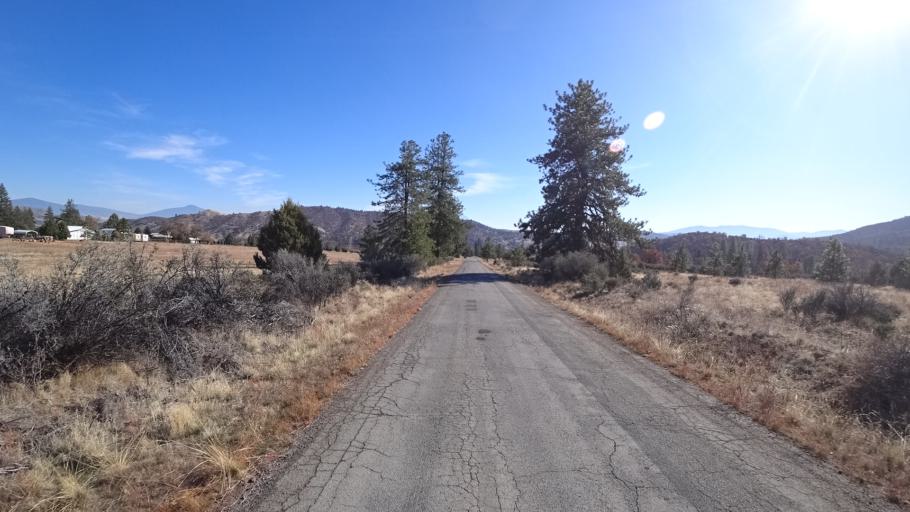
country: US
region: California
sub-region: Siskiyou County
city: Yreka
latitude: 41.7700
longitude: -122.6331
